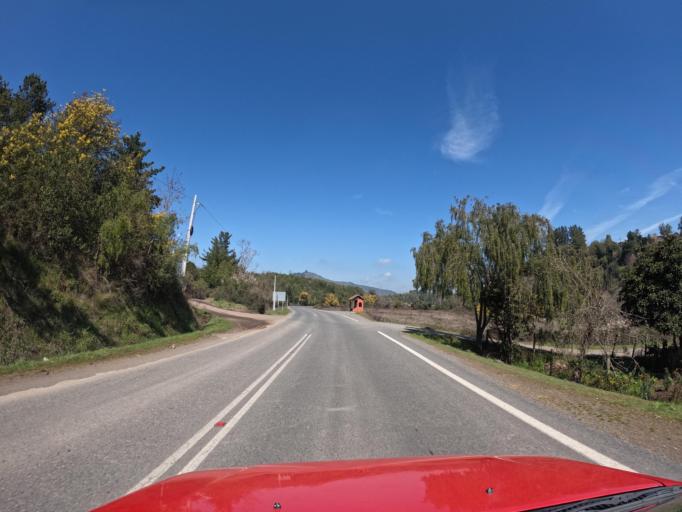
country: CL
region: Maule
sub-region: Provincia de Talca
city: San Clemente
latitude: -35.4609
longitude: -71.2698
